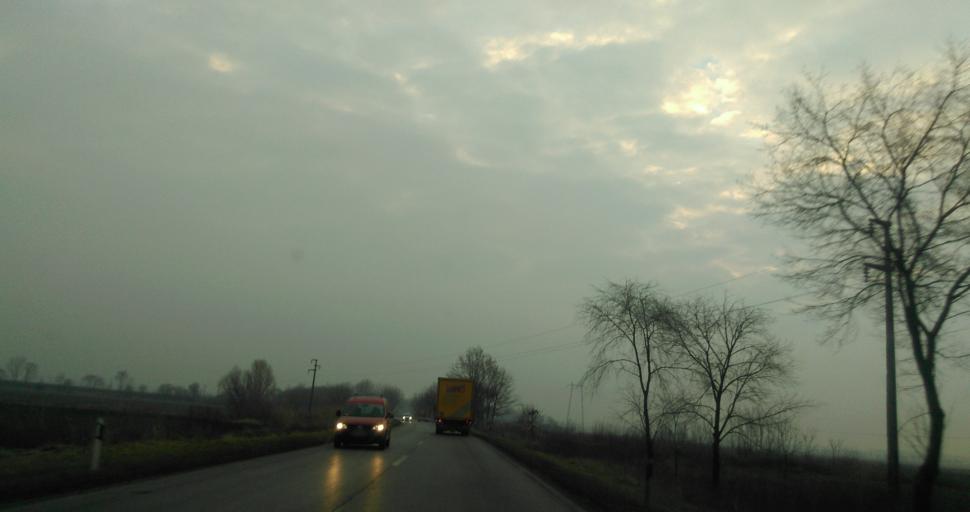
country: RS
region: Autonomna Pokrajina Vojvodina
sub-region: Juznobacki Okrug
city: Becej
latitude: 45.5820
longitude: 20.0728
